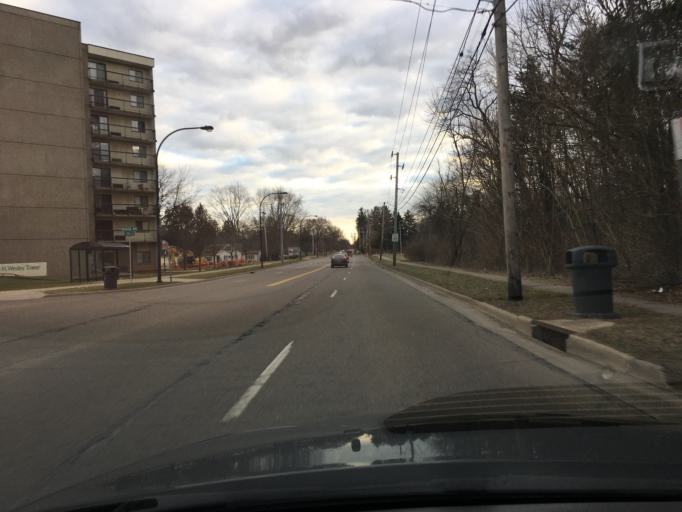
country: US
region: Ohio
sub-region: Summit County
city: Fairlawn
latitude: 41.1080
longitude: -81.5693
